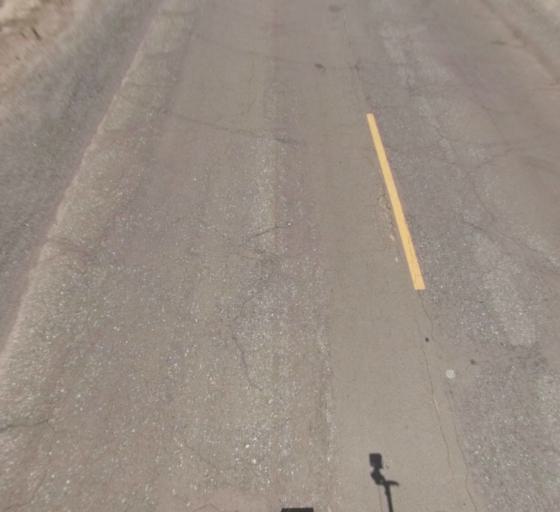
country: US
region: California
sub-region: Madera County
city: Parksdale
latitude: 36.8841
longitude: -119.9836
